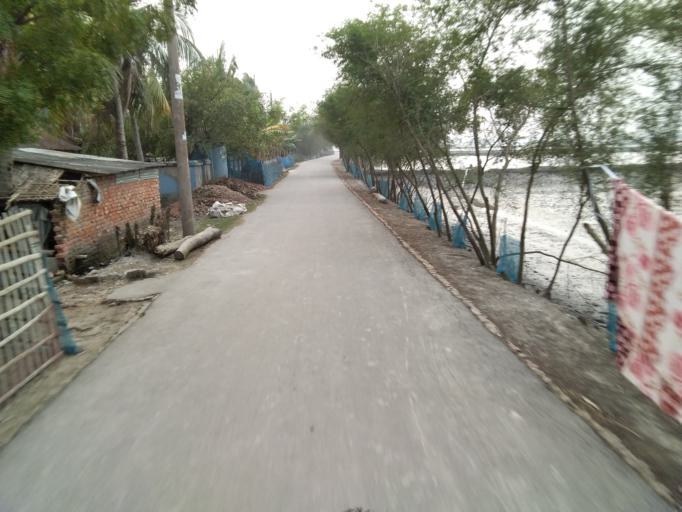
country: BD
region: Khulna
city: Satkhira
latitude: 22.5839
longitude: 89.0595
